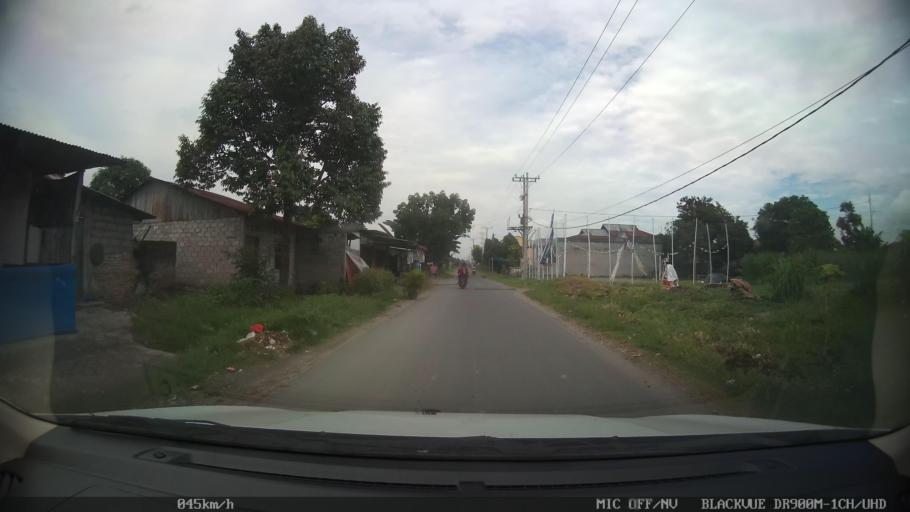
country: ID
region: North Sumatra
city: Sunggal
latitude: 3.6144
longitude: 98.5973
